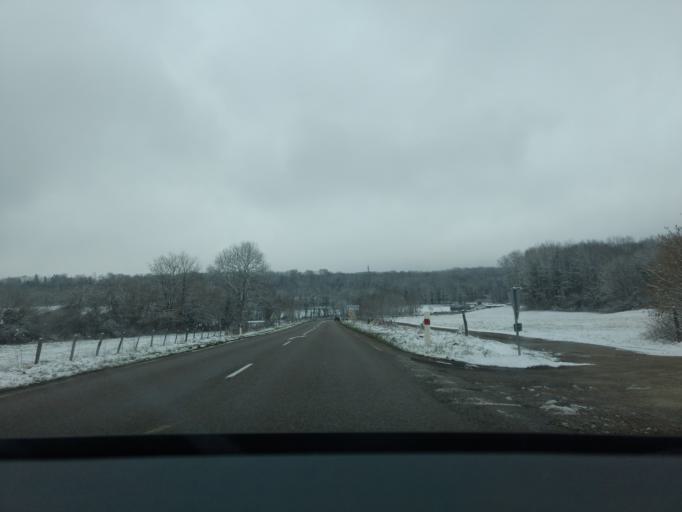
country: FR
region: Franche-Comte
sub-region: Departement du Jura
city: Champagnole
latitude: 46.8046
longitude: 5.8268
